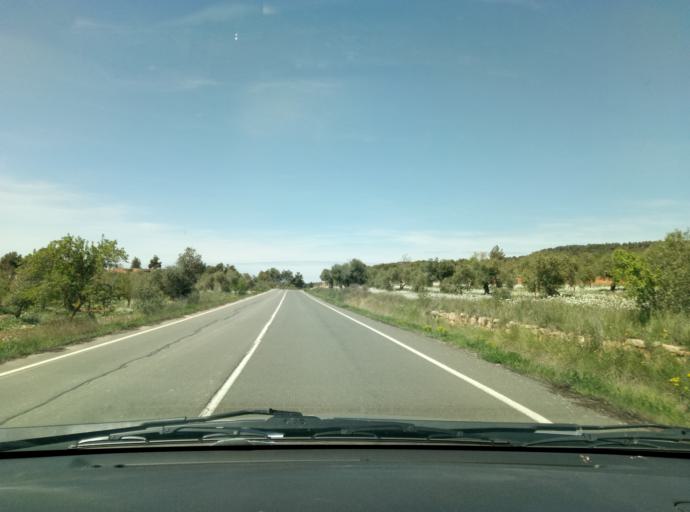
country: ES
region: Catalonia
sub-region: Provincia de Lleida
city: Vinaixa
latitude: 41.4254
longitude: 0.9073
